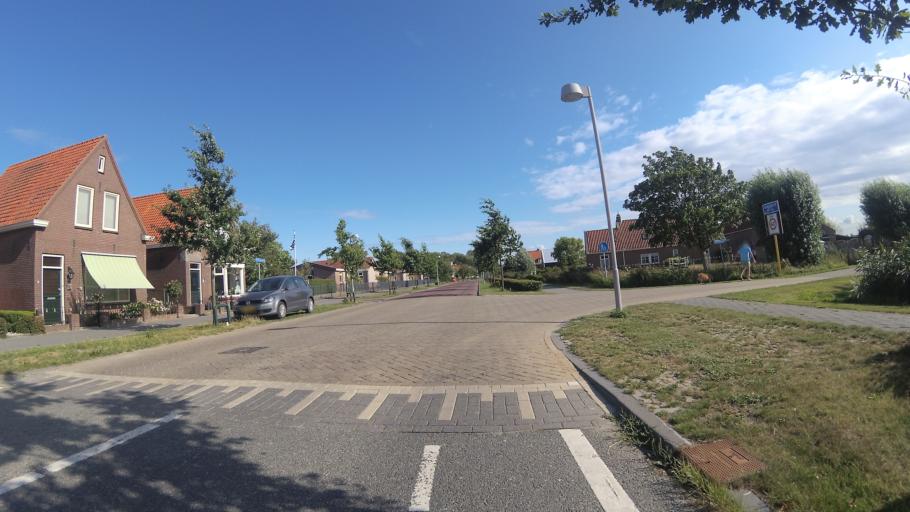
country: NL
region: Zeeland
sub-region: Gemeente Middelburg
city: Middelburg
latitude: 51.5547
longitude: 3.5866
